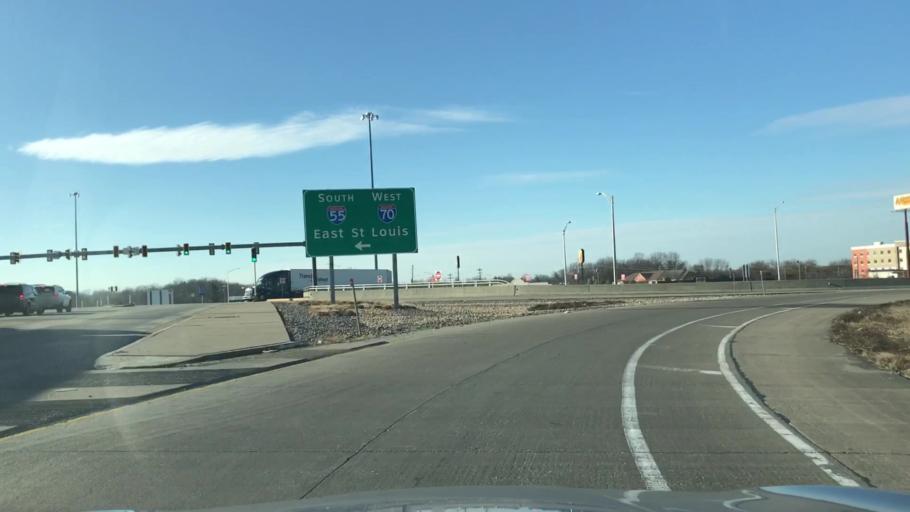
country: US
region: Illinois
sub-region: Madison County
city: Troy
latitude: 38.7325
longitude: -89.9115
